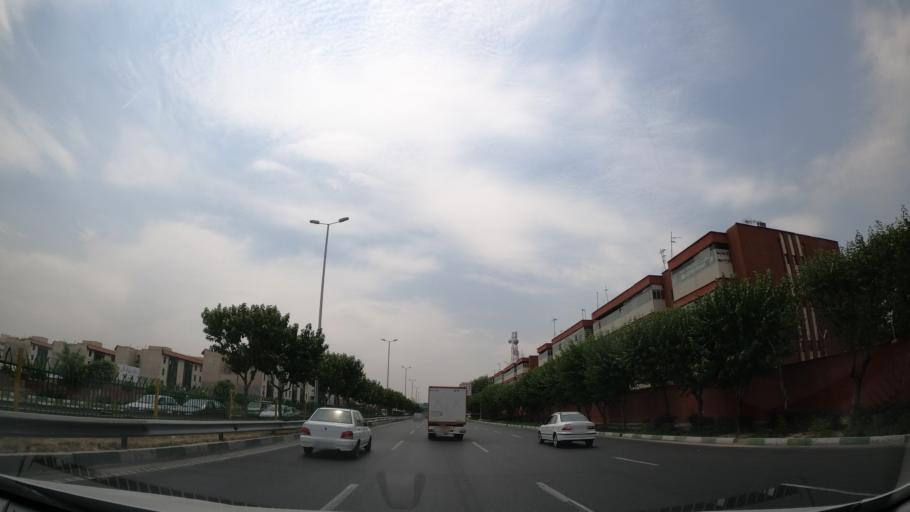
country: IR
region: Tehran
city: Tehran
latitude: 35.6784
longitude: 51.3307
